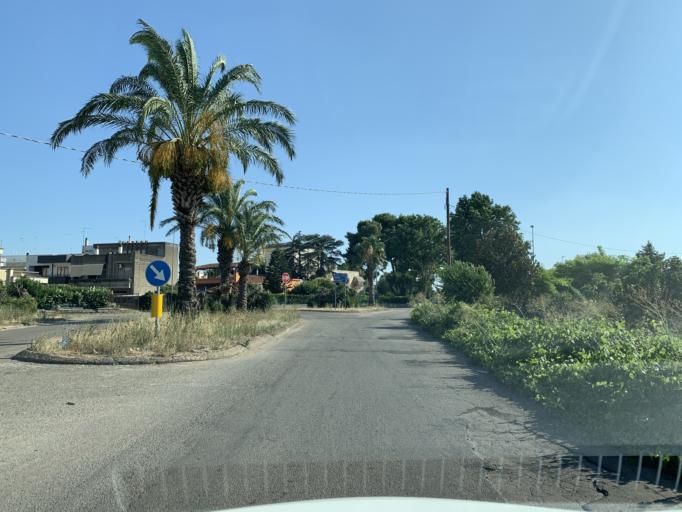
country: IT
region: Apulia
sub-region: Provincia di Lecce
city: Nardo
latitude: 40.1854
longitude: 18.0389
